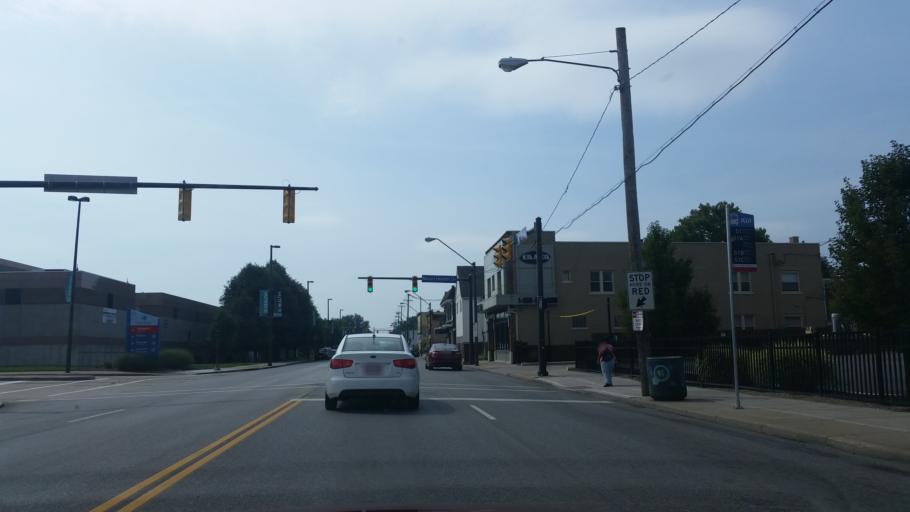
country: US
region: Ohio
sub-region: Cuyahoga County
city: Cleveland
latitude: 41.4634
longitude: -81.7005
